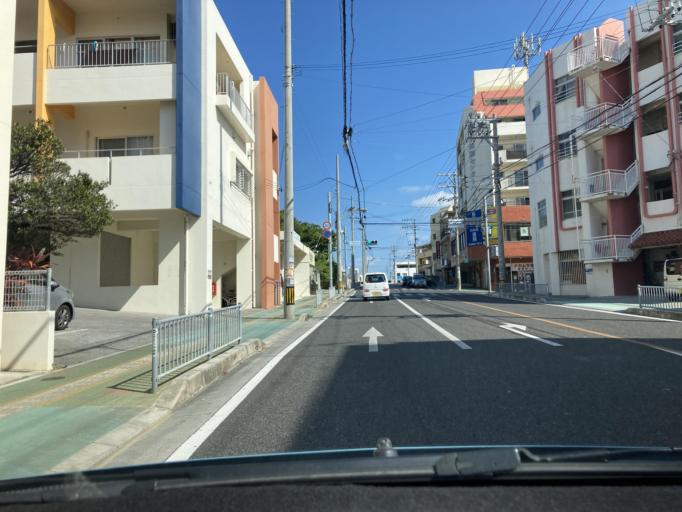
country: JP
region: Okinawa
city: Tomigusuku
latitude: 26.1879
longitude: 127.6676
